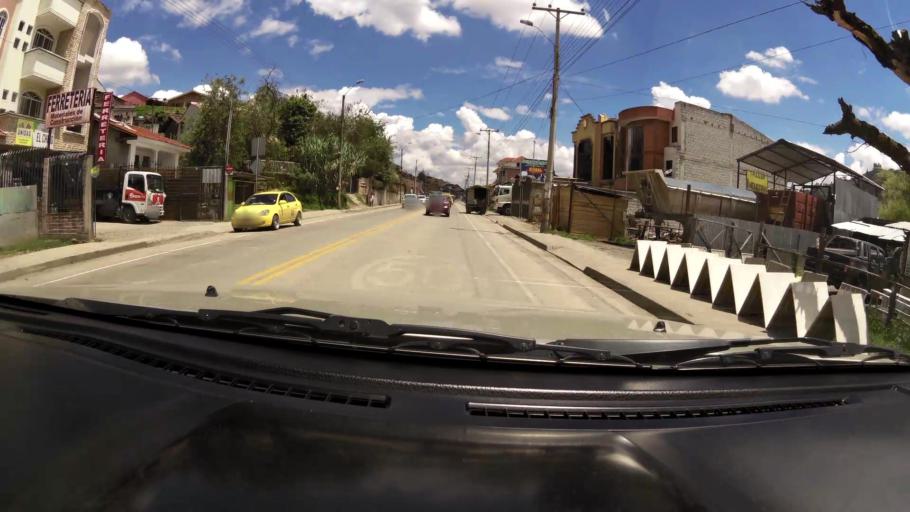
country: EC
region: Azuay
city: Cuenca
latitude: -2.9369
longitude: -79.0460
